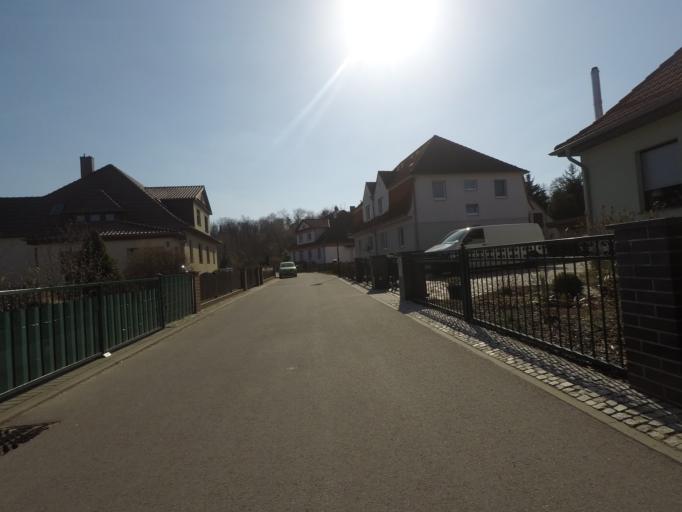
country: DE
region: Brandenburg
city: Eberswalde
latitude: 52.8392
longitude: 13.7962
